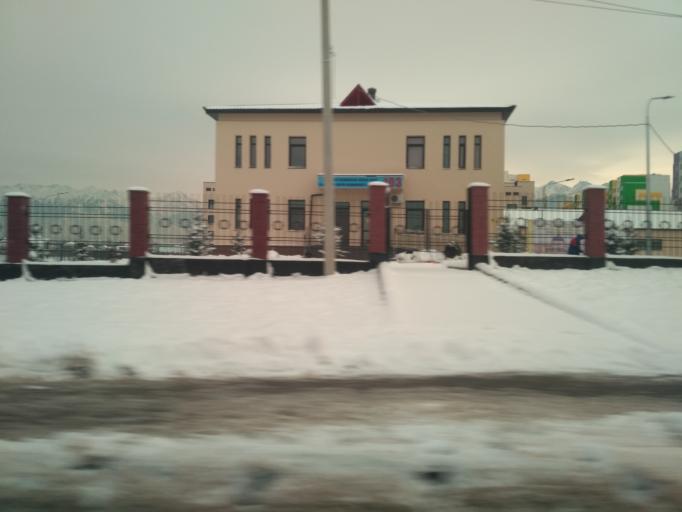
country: KZ
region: Almaty Qalasy
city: Almaty
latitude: 43.2154
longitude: 76.7901
